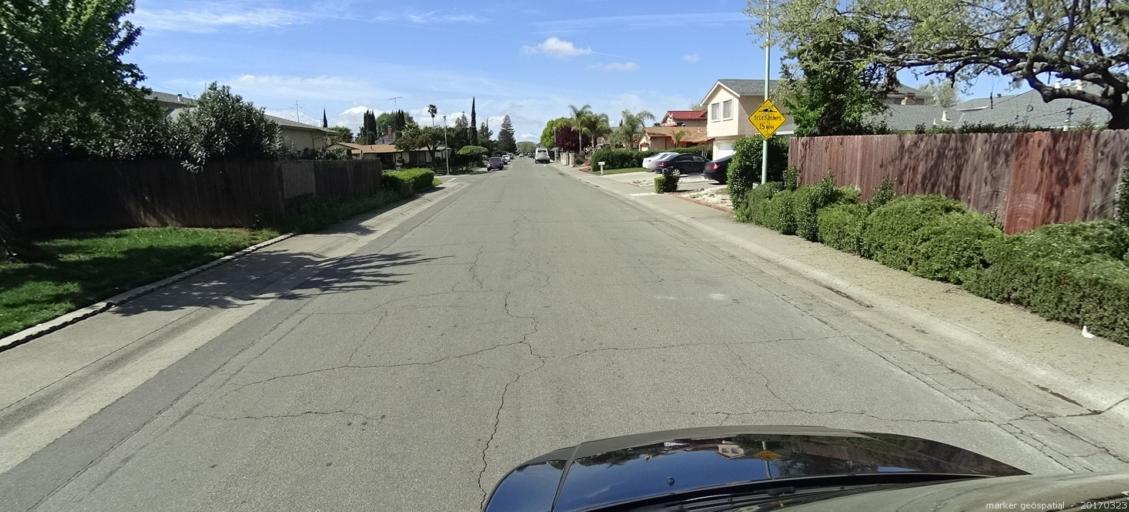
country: US
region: California
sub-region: Sacramento County
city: Florin
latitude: 38.5098
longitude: -121.4228
